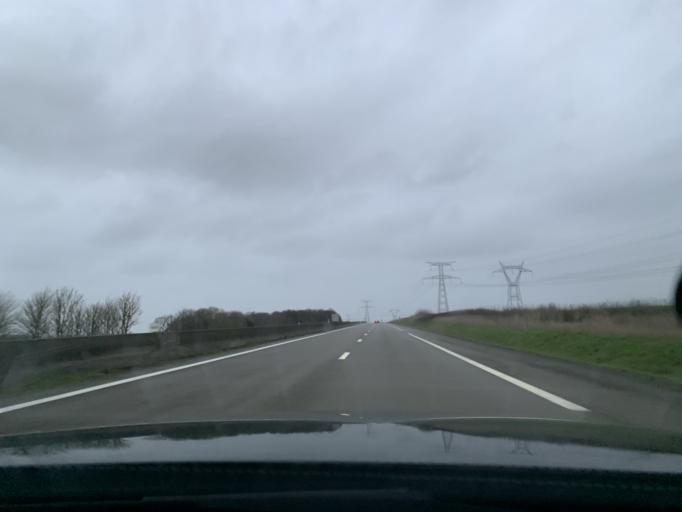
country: FR
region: Picardie
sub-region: Departement de la Somme
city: Saleux
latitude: 49.7763
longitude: 2.2360
